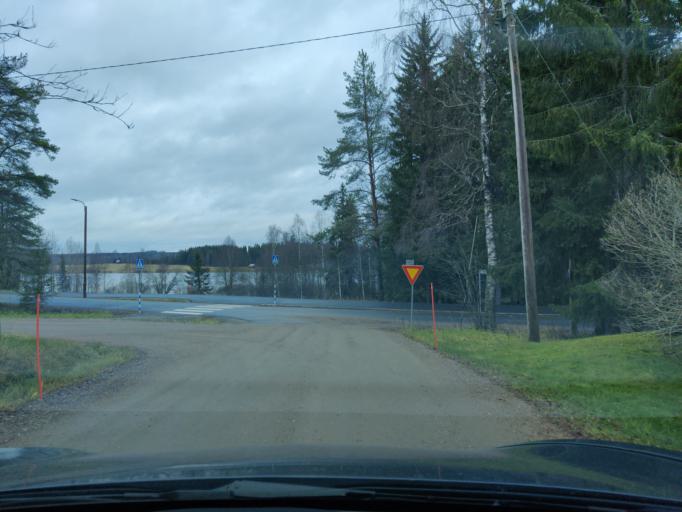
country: FI
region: Northern Savo
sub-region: Ylae-Savo
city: Kiuruvesi
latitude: 63.6463
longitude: 26.6404
